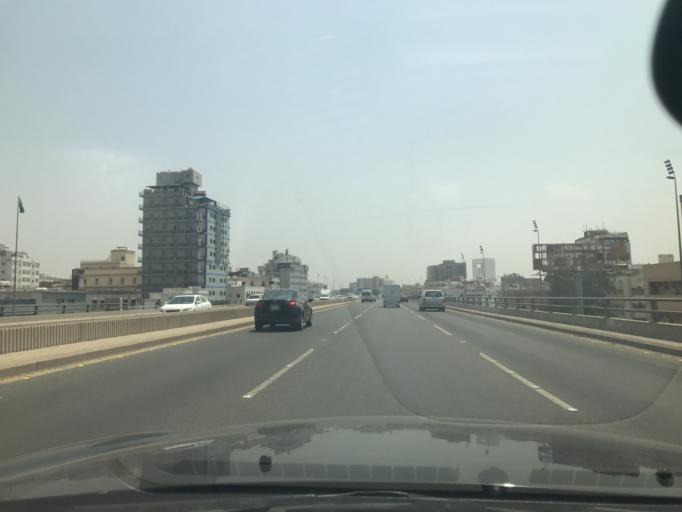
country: SA
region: Makkah
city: Jeddah
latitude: 21.4771
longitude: 39.1847
